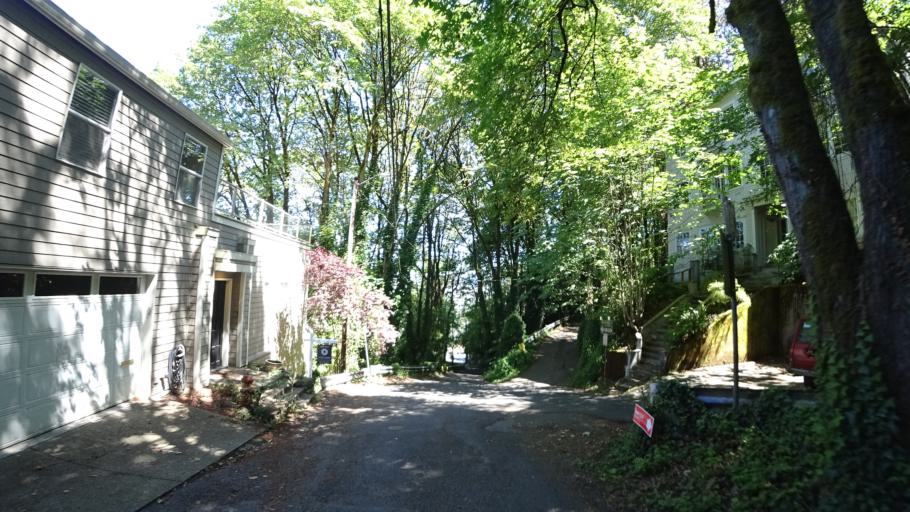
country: US
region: Oregon
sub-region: Multnomah County
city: Portland
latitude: 45.5117
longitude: -122.6906
